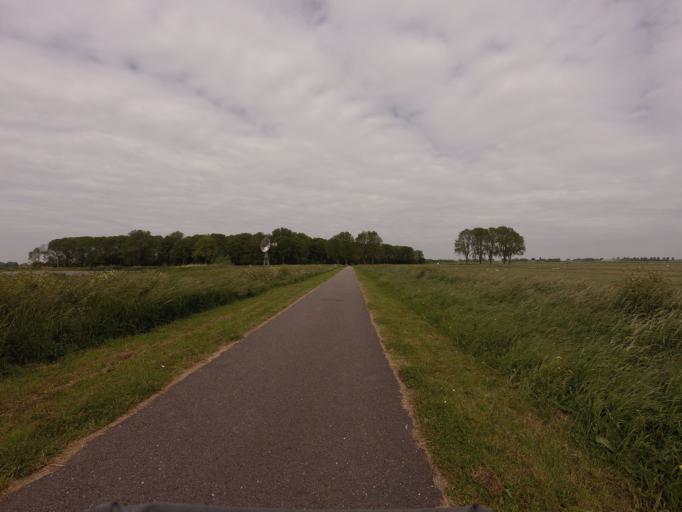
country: NL
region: North Holland
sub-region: Gemeente Medemblik
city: Opperdoes
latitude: 52.7141
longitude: 5.1008
